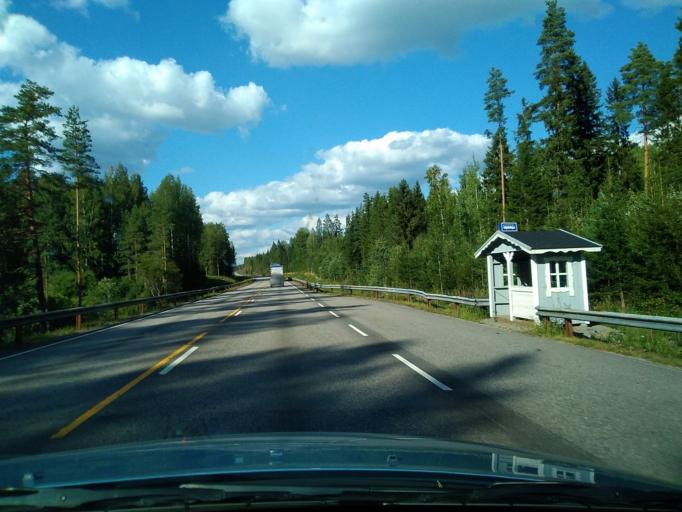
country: FI
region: Central Finland
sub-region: Keuruu
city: Keuruu
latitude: 62.1383
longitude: 24.7417
